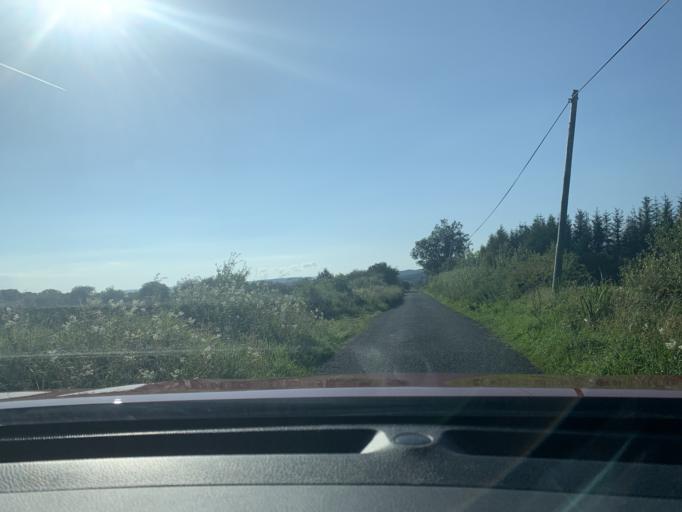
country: IE
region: Connaught
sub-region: Sligo
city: Tobercurry
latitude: 54.0753
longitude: -8.7854
